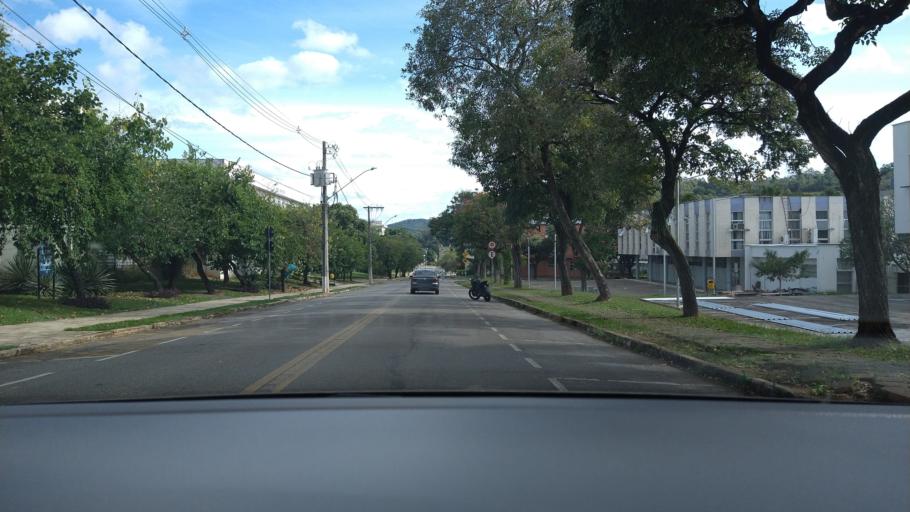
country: BR
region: Minas Gerais
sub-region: Vicosa
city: Vicosa
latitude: -20.7610
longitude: -42.8658
